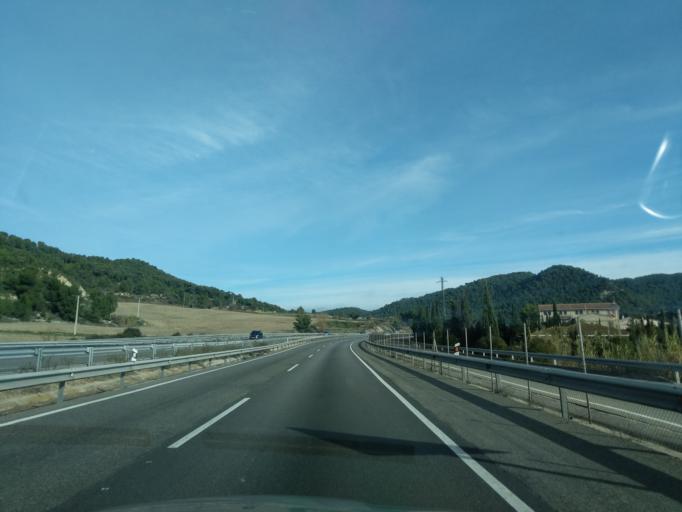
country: ES
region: Catalonia
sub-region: Provincia de Barcelona
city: Castelloli
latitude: 41.5973
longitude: 1.6964
